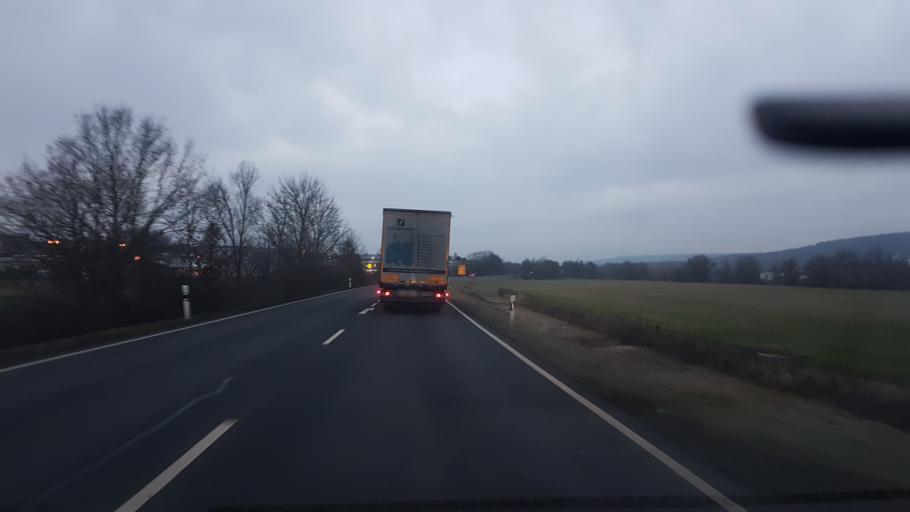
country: DE
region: Bavaria
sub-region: Regierungsbezirk Unterfranken
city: Rentweinsdorf
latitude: 50.0868
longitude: 10.7896
